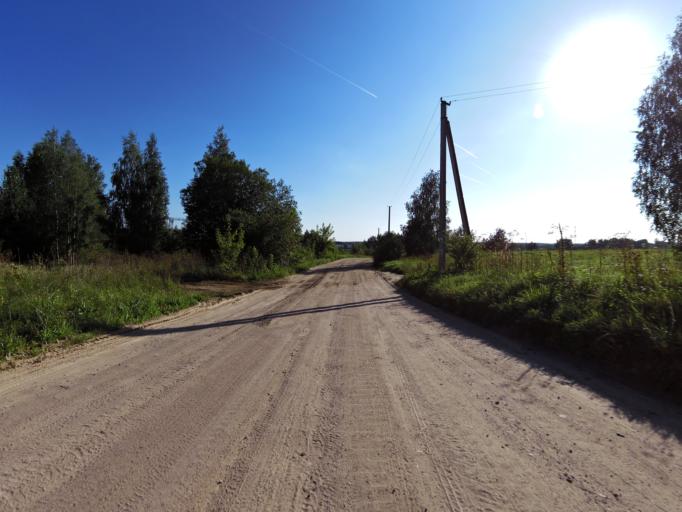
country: LT
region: Vilnius County
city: Pilaite
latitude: 54.7127
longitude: 25.1749
